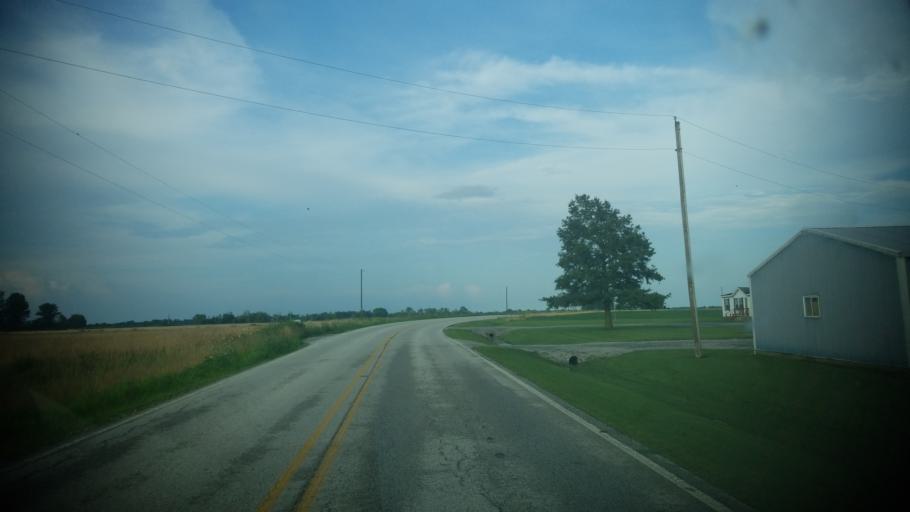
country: US
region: Illinois
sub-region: Clay County
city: Flora
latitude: 38.5170
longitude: -88.4838
